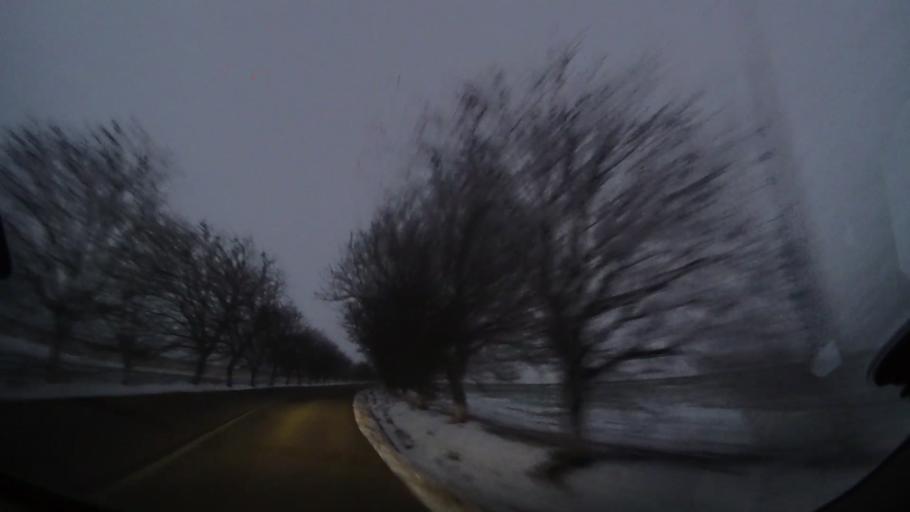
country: RO
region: Vaslui
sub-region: Comuna Dimitrie Cantemir
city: Dimitrie Cantemir
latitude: 46.5142
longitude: 28.0315
